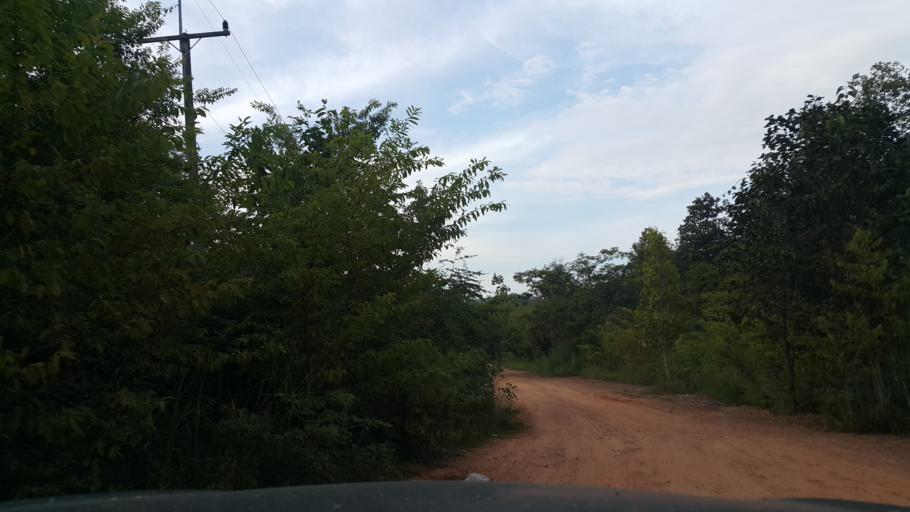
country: TH
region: Chiang Mai
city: San Sai
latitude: 18.9245
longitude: 99.0646
